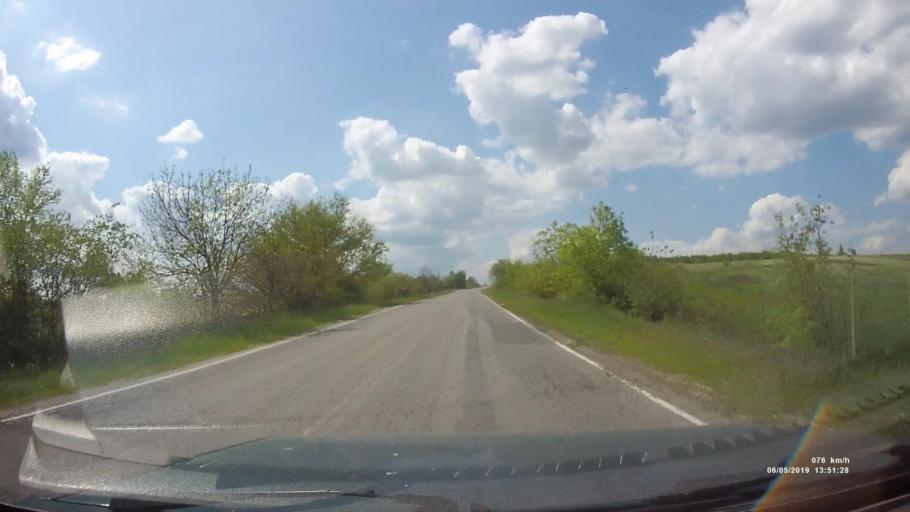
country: RU
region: Rostov
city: Melikhovskaya
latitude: 47.6572
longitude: 40.4914
